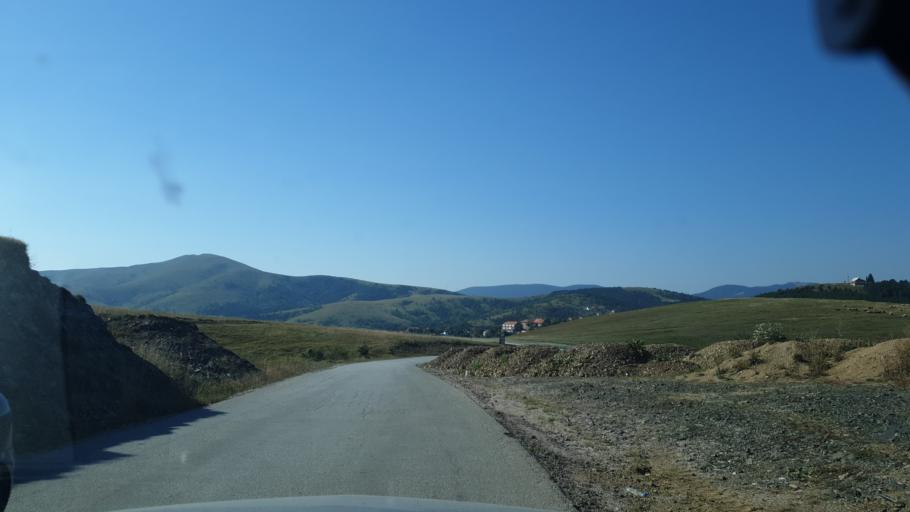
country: RS
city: Zlatibor
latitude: 43.7182
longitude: 19.7217
